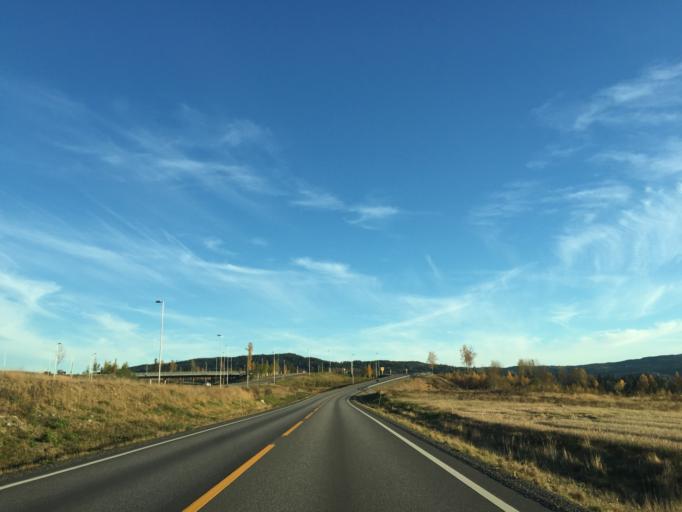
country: NO
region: Hedmark
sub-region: Kongsvinger
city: Spetalen
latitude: 60.2103
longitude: 11.8852
